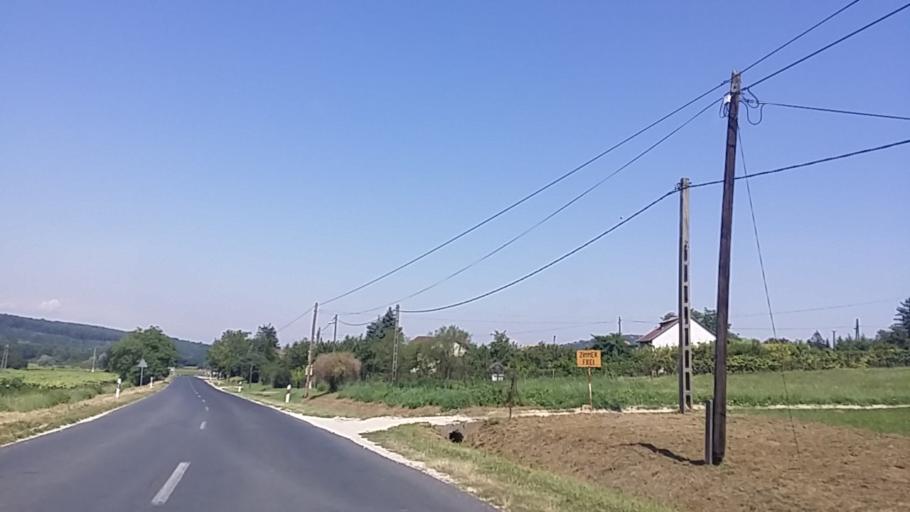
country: HU
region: Zala
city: Cserszegtomaj
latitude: 46.8077
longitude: 17.2061
